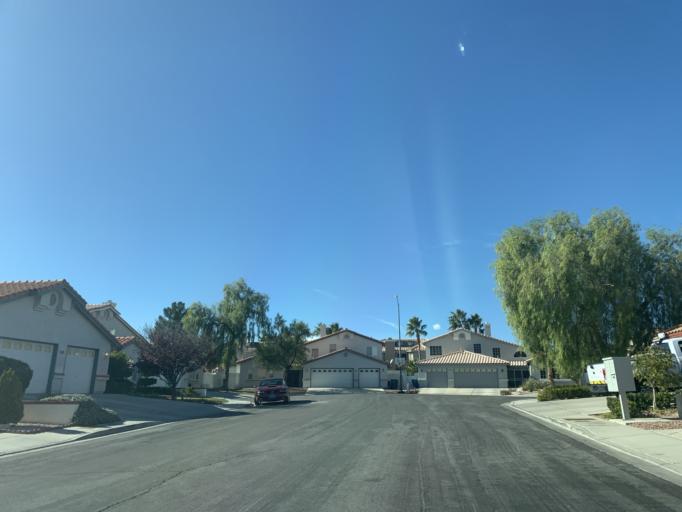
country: US
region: Nevada
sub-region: Clark County
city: Summerlin South
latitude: 36.1228
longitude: -115.2882
